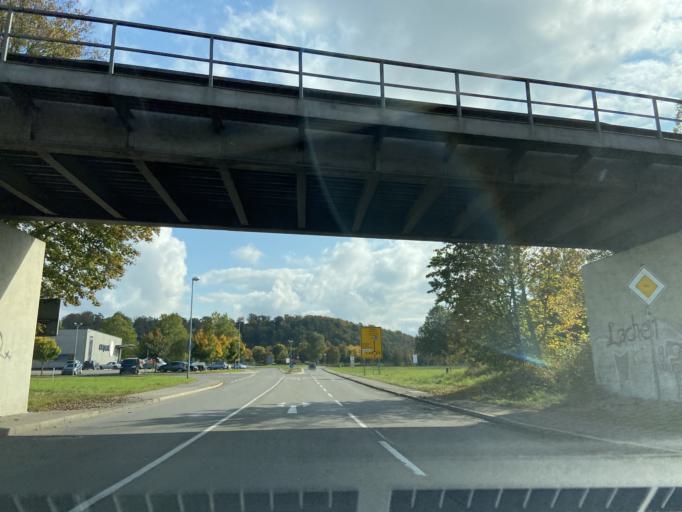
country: DE
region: Baden-Wuerttemberg
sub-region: Tuebingen Region
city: Sigmaringen
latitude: 48.0866
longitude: 9.2032
